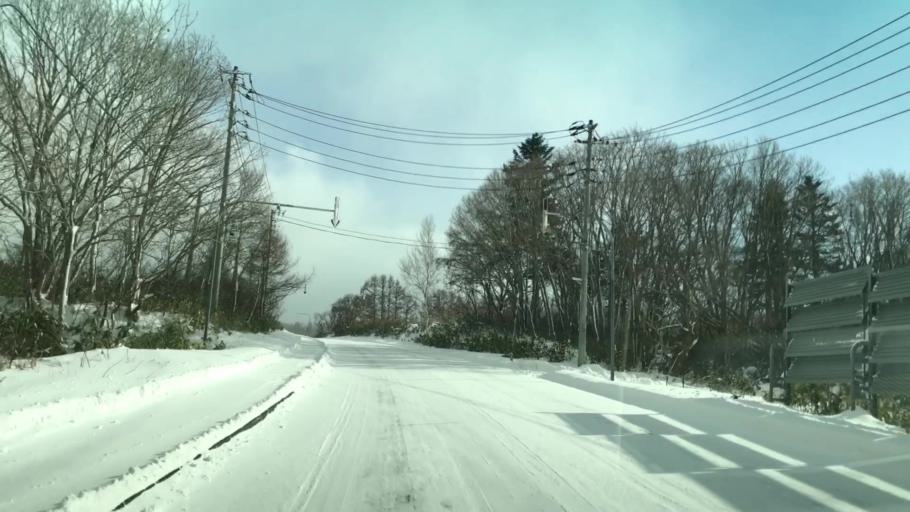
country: JP
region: Hokkaido
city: Yoichi
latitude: 43.3053
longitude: 140.5580
